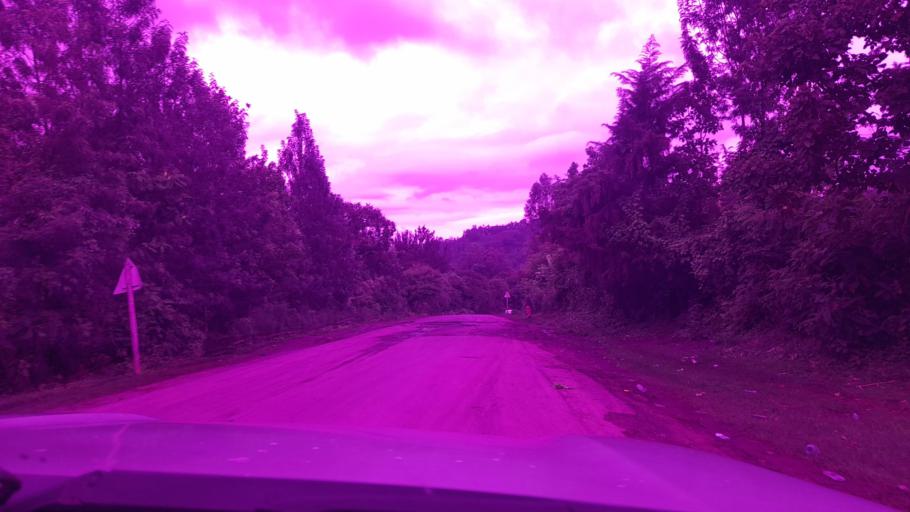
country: ET
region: Oromiya
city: Jima
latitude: 7.9209
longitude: 37.4053
